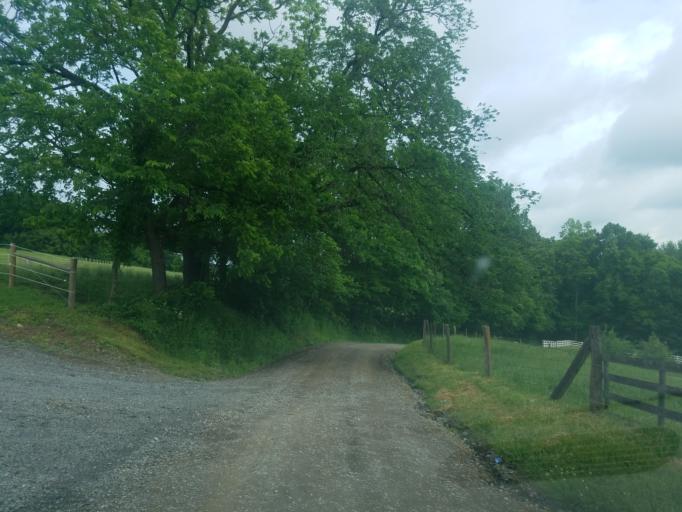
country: US
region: Ohio
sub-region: Holmes County
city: Millersburg
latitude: 40.4823
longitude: -81.8138
